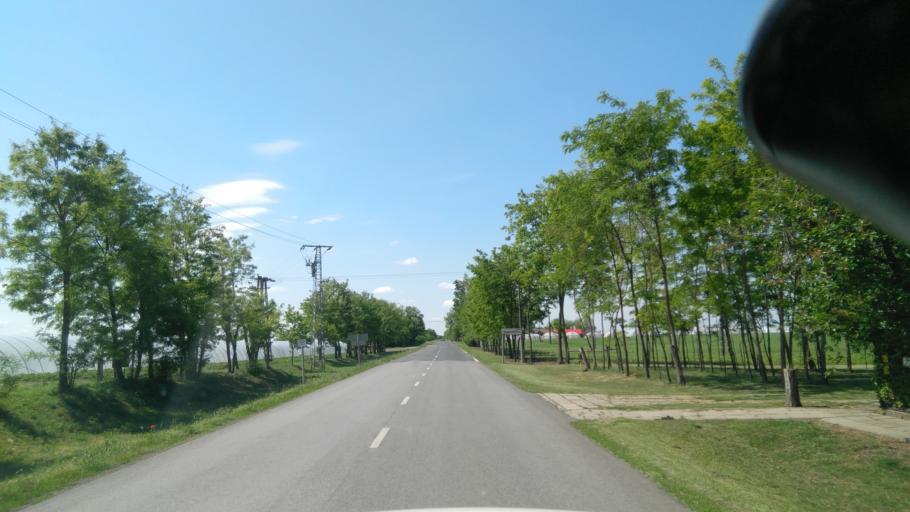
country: HU
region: Bekes
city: Medgyesegyhaza
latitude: 46.4868
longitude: 21.0249
